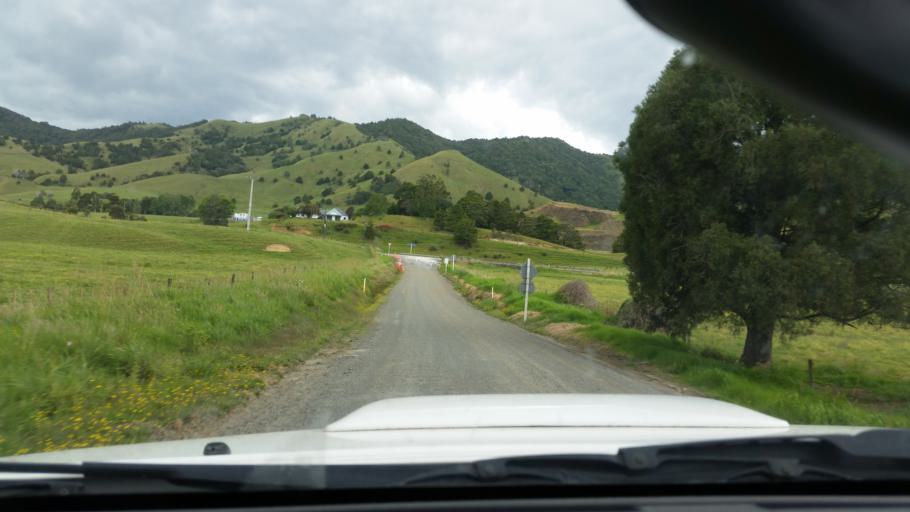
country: NZ
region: Northland
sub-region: Kaipara District
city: Dargaville
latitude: -35.8021
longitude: 173.9165
